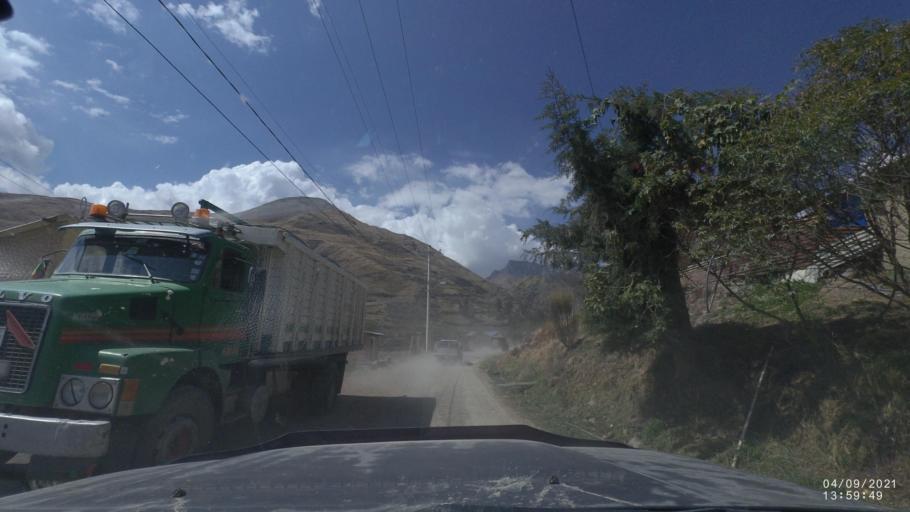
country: BO
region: Cochabamba
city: Sipe Sipe
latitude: -17.2319
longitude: -66.4871
